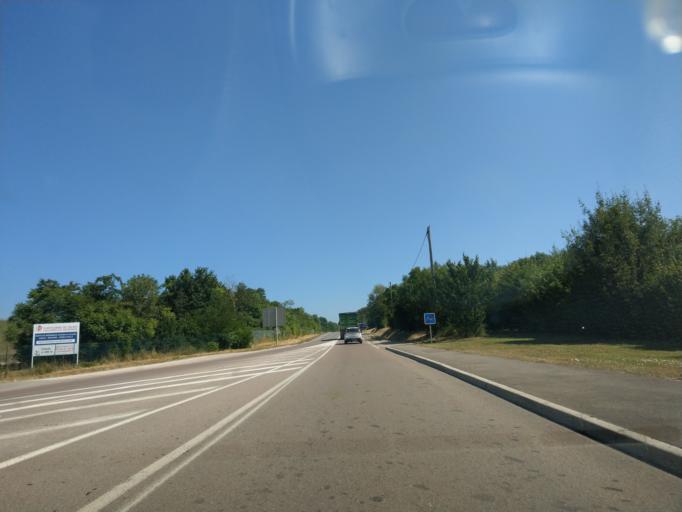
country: FR
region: Bourgogne
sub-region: Departement de la Cote-d'Or
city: Ahuy
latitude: 47.3672
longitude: 5.0475
